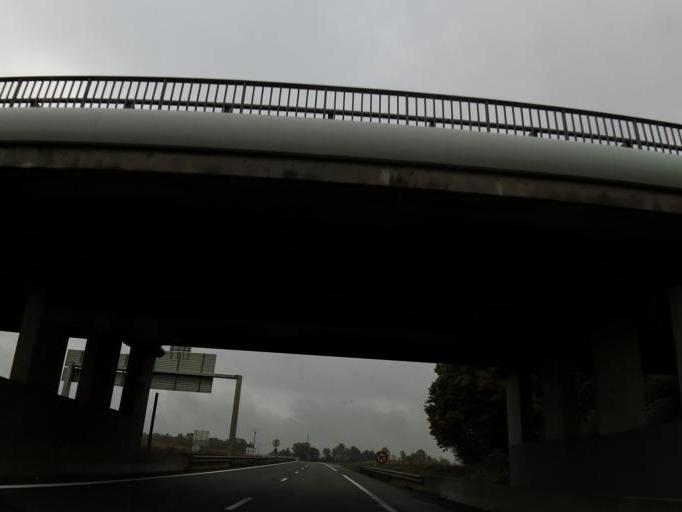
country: FR
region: Ile-de-France
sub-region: Departement de Seine-et-Marne
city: Chamigny
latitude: 49.0122
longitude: 3.1503
